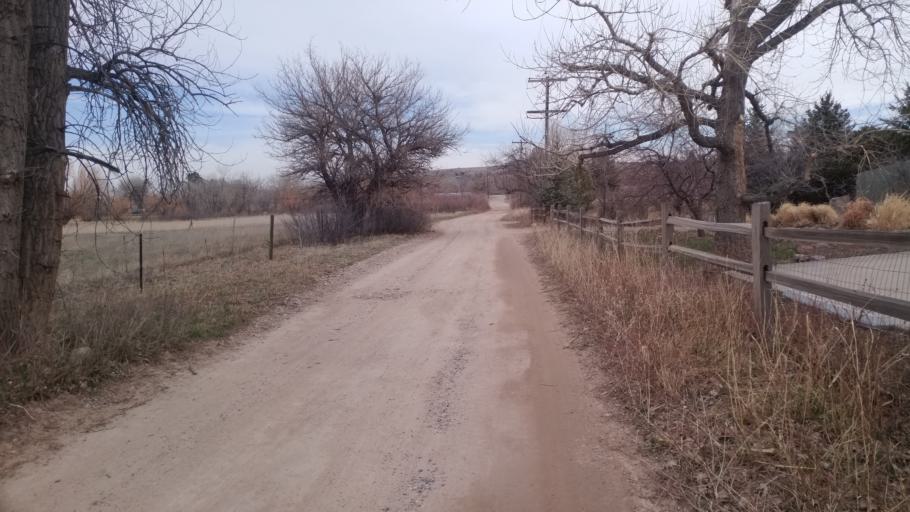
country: US
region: Colorado
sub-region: Boulder County
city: Boulder
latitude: 39.9605
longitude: -105.2397
